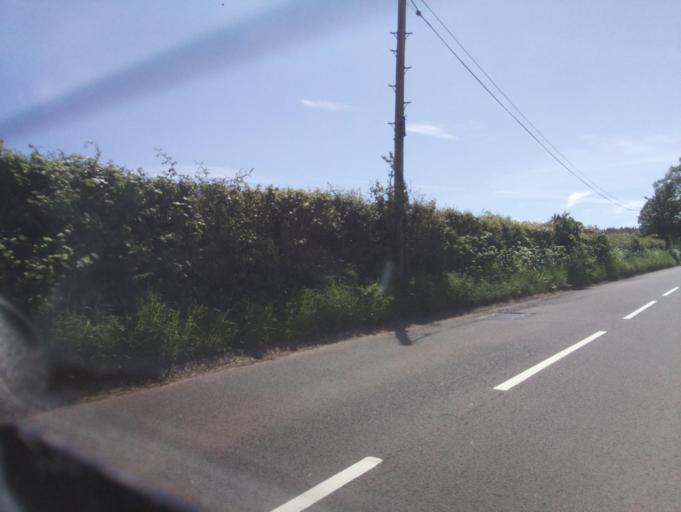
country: GB
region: Wales
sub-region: Monmouthshire
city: Mitchel Troy
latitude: 51.7247
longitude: -2.7574
